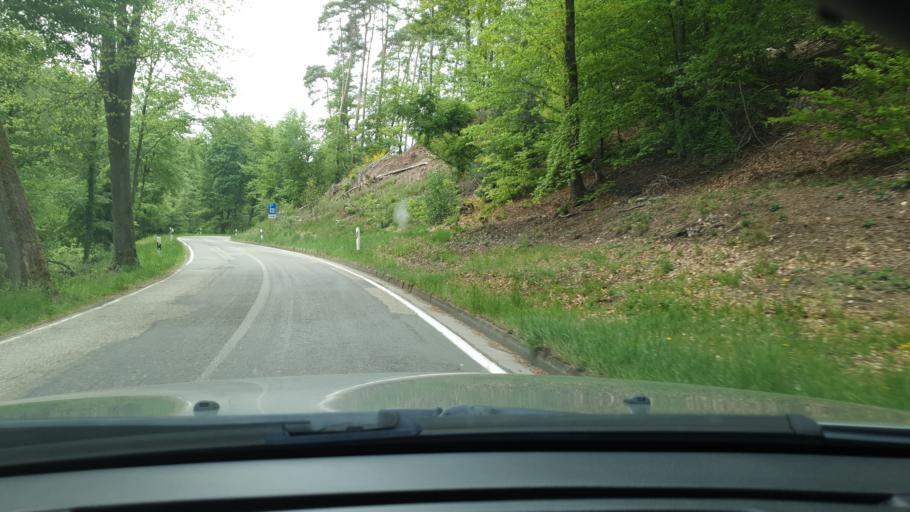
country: DE
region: Rheinland-Pfalz
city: Martinshohe
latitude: 49.3774
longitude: 7.4838
